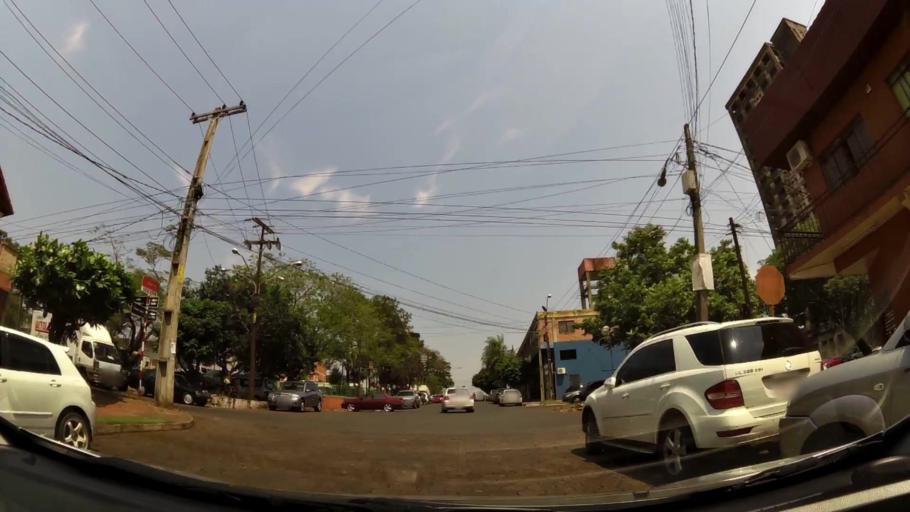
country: PY
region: Alto Parana
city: Presidente Franco
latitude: -25.5258
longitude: -54.6096
